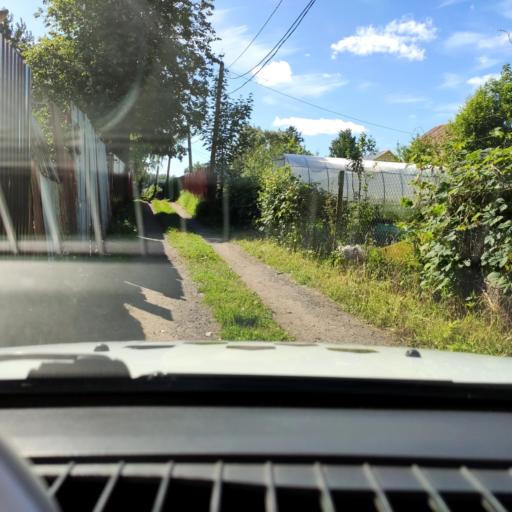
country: RU
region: Perm
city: Kondratovo
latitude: 58.0581
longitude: 56.1330
